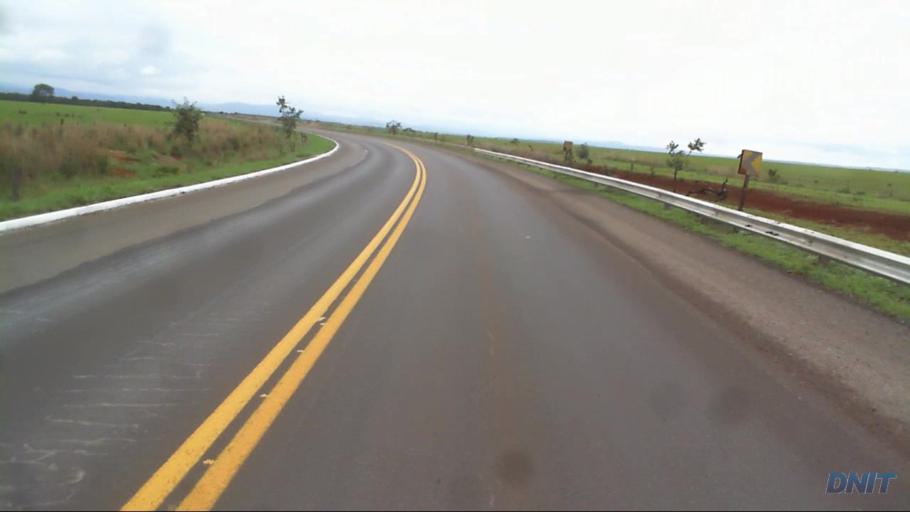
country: BR
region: Goias
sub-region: Padre Bernardo
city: Padre Bernardo
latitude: -15.1735
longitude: -48.3695
